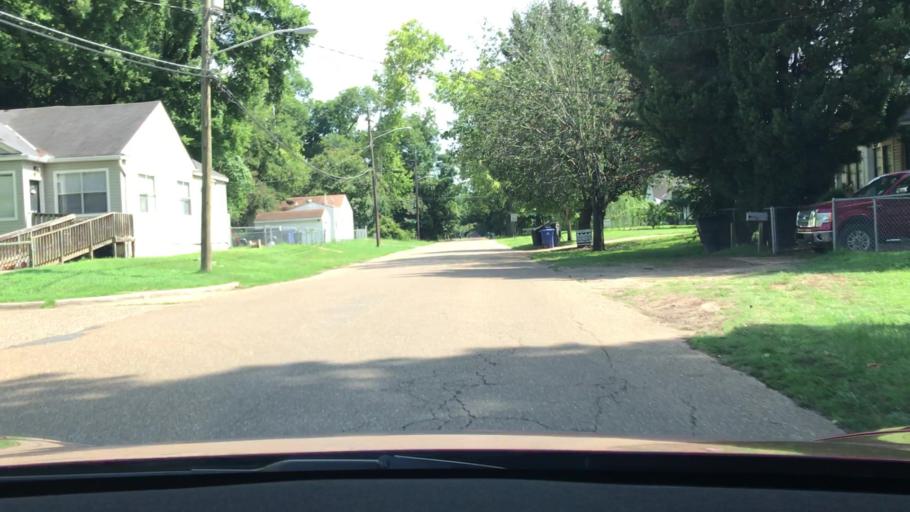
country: US
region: Louisiana
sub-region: Bossier Parish
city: Bossier City
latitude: 32.4773
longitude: -93.7312
